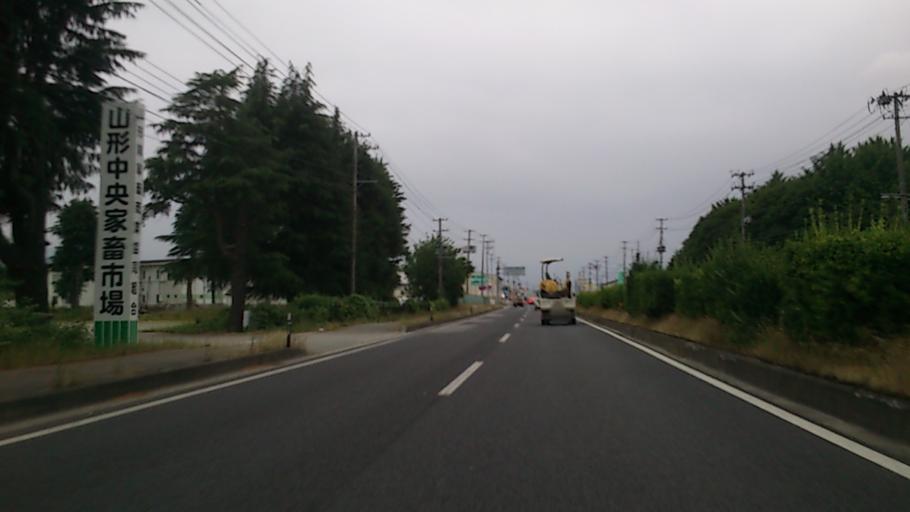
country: JP
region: Yamagata
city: Tendo
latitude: 38.3378
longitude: 140.3716
